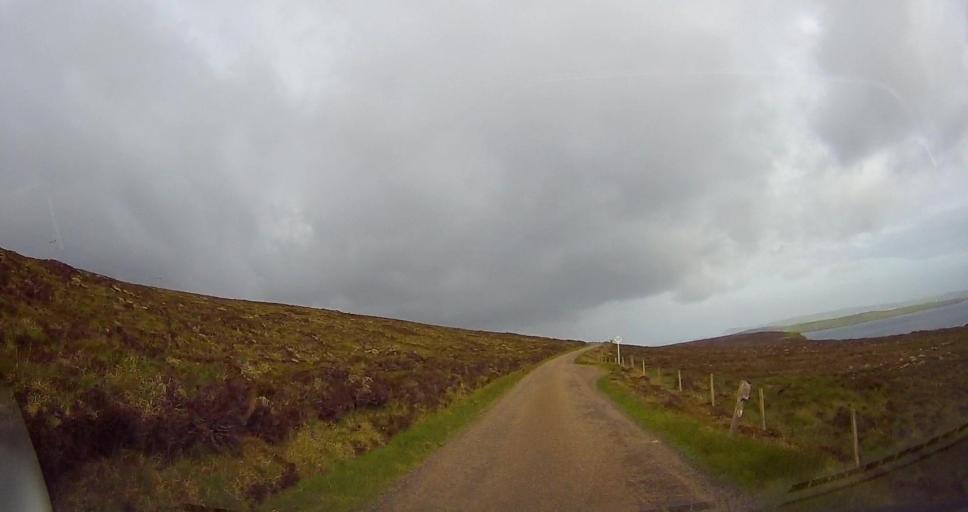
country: GB
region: Scotland
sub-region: Orkney Islands
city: Stromness
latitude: 58.8917
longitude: -3.2610
